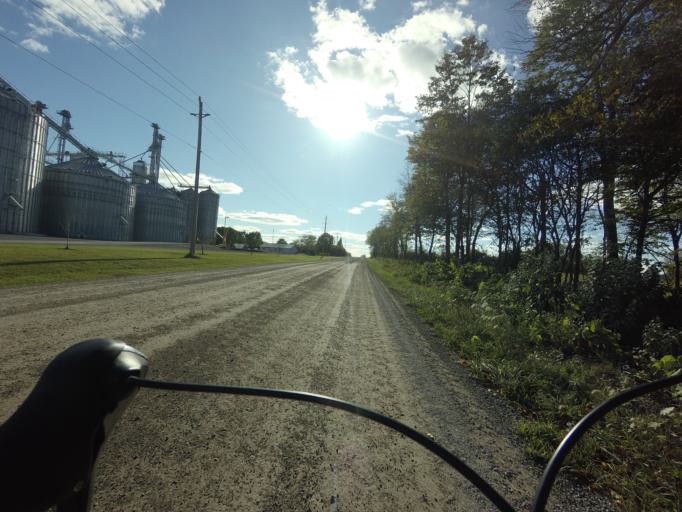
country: CA
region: Ontario
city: Bells Corners
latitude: 45.1123
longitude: -75.7125
